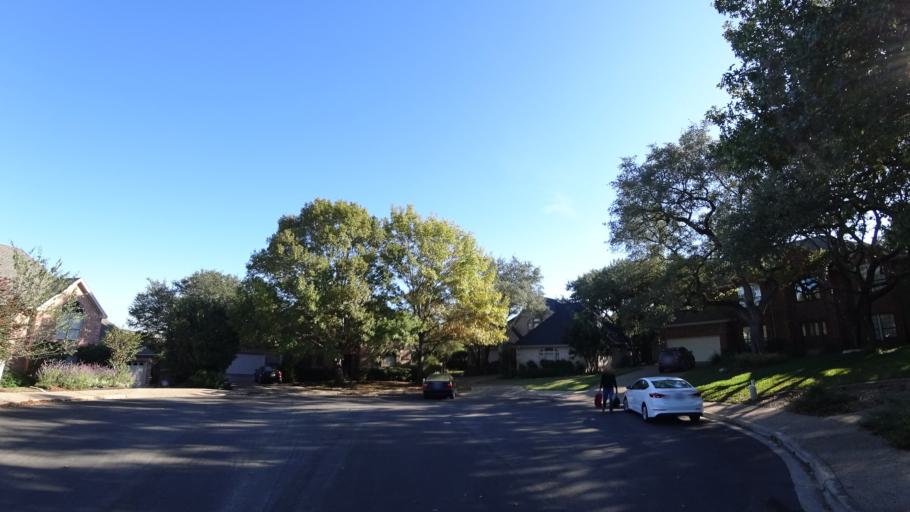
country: US
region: Texas
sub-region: Williamson County
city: Jollyville
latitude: 30.4140
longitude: -97.7786
